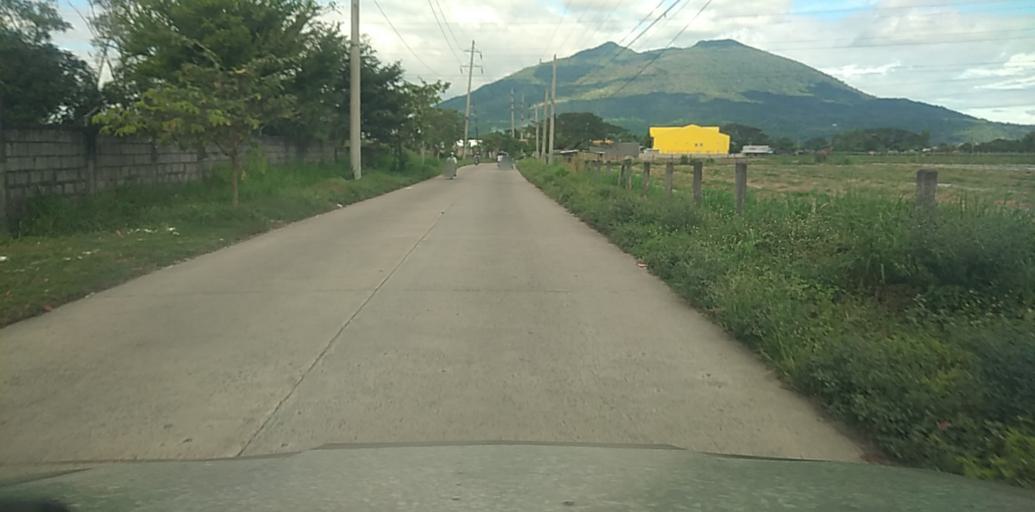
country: PH
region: Central Luzon
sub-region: Province of Pampanga
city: Arenas
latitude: 15.1750
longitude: 120.6762
